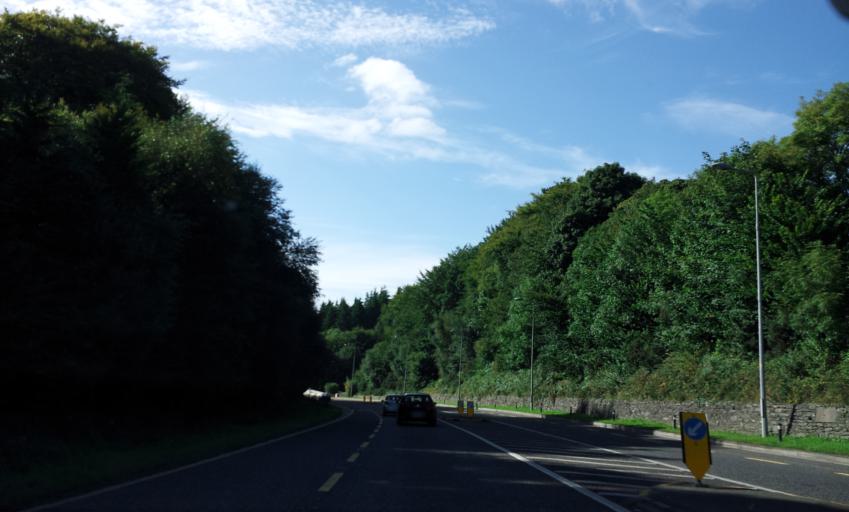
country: IE
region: Munster
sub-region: Ciarrai
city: Cill Airne
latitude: 52.0562
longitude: -9.4664
